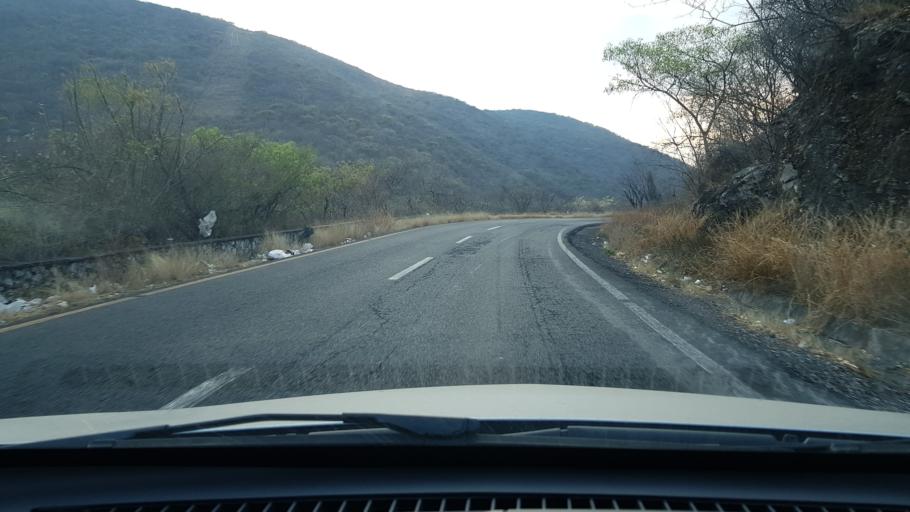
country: MX
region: Morelos
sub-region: Jiutepec
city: Independencia
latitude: 18.8583
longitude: -99.1166
